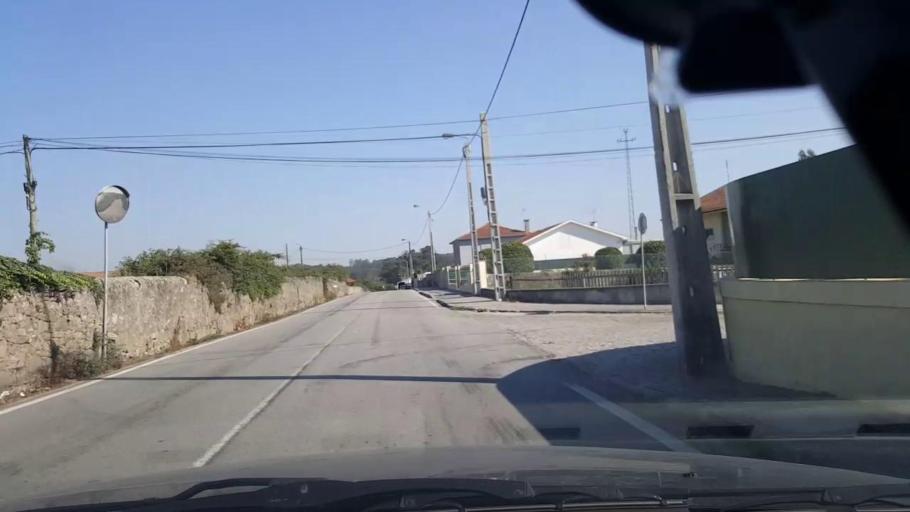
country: PT
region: Porto
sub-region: Vila do Conde
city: Arvore
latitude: 41.3449
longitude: -8.6797
